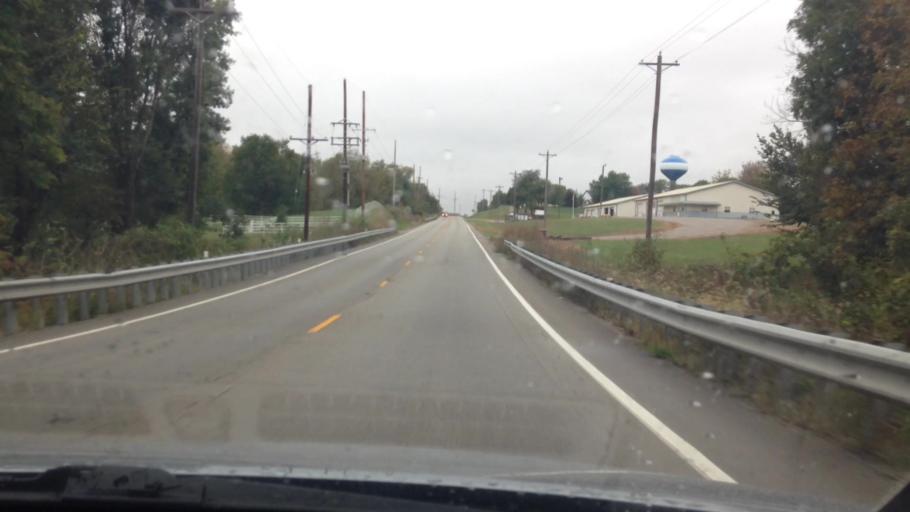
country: US
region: Missouri
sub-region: Platte County
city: Weston
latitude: 39.4127
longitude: -94.8815
